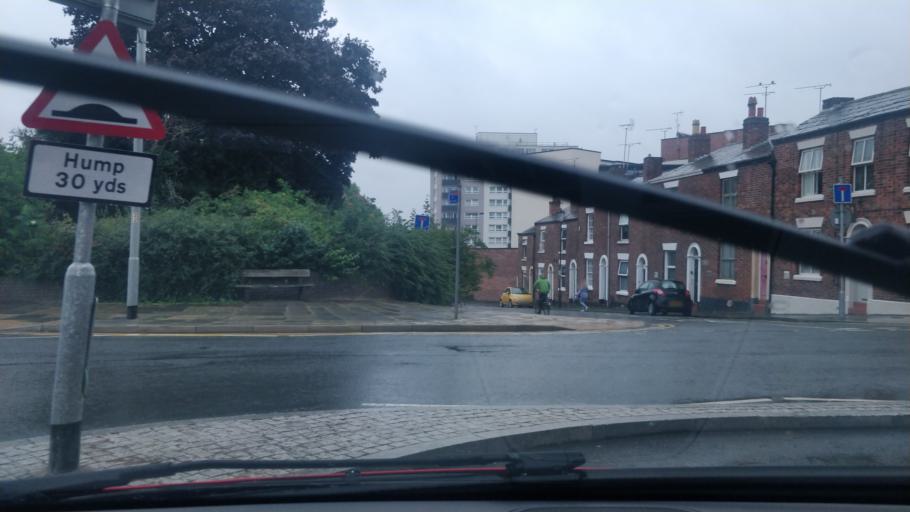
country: GB
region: England
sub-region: Cheshire West and Chester
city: Chester
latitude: 53.1952
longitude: -2.8921
